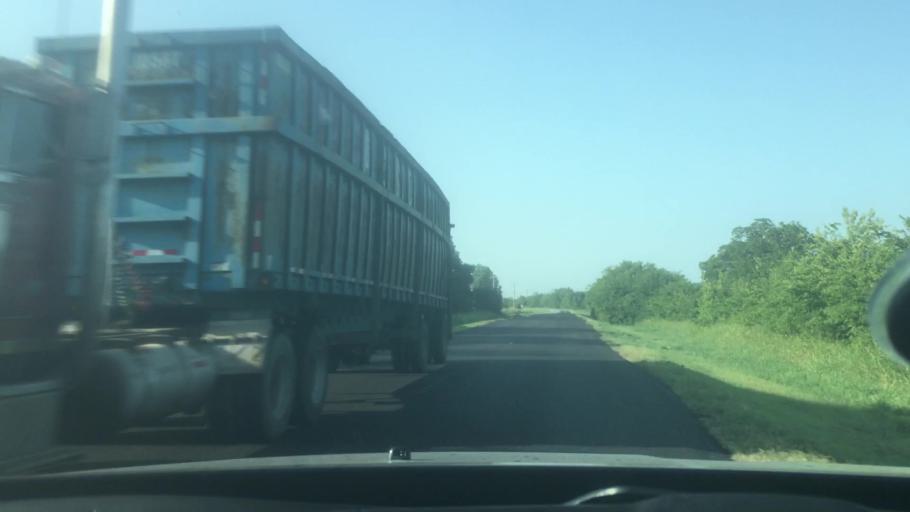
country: US
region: Oklahoma
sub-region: Coal County
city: Coalgate
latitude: 34.3551
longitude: -96.4246
